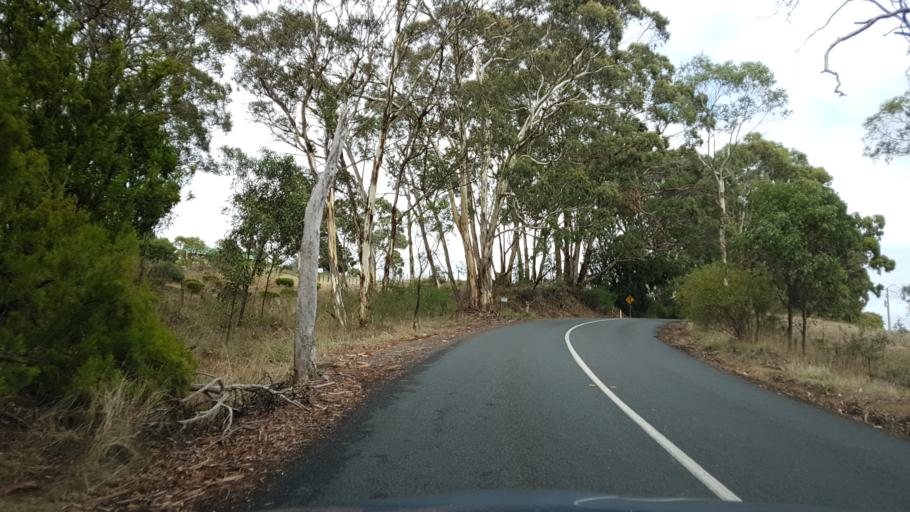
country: AU
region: South Australia
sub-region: Mount Barker
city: Little Hampton
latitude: -35.0795
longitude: 138.8257
